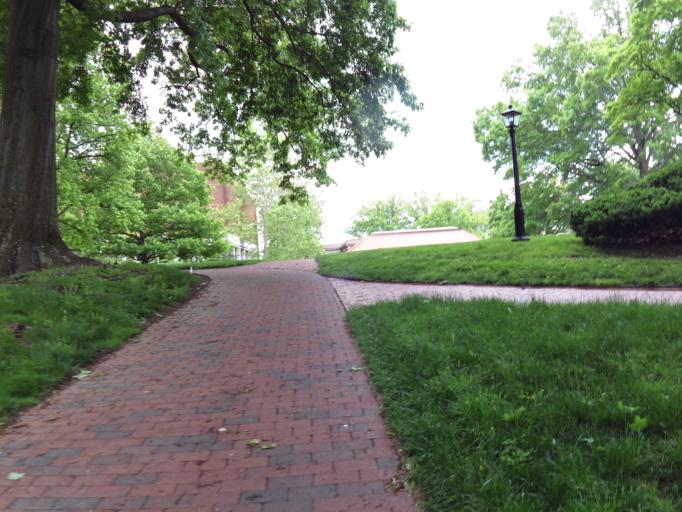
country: US
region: Ohio
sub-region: Athens County
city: Athens
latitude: 39.3264
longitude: -82.1007
